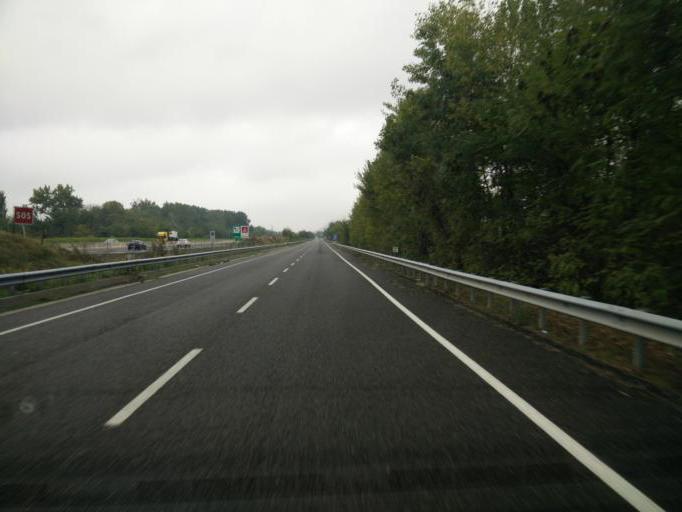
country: IT
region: Emilia-Romagna
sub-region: Provincia di Bologna
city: Borgonuovo
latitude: 44.4371
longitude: 11.2780
